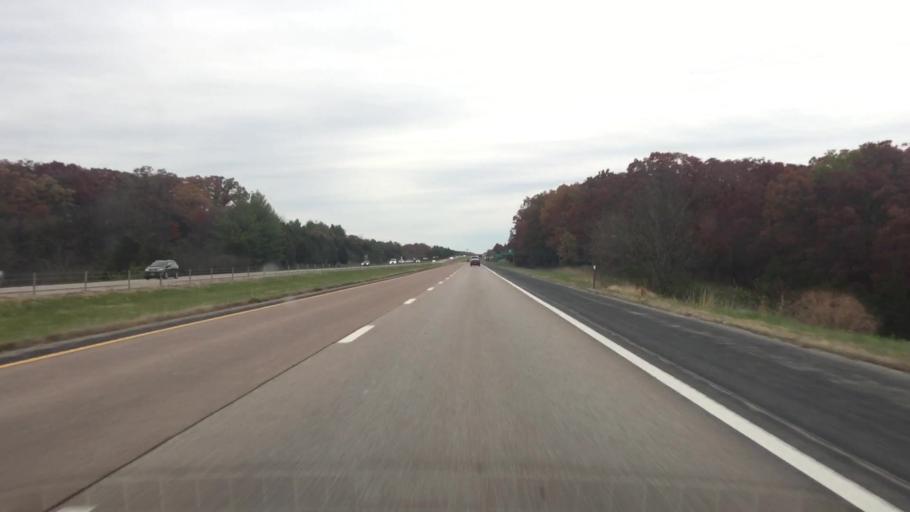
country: US
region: Missouri
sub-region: Boone County
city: Ashland
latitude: 38.7260
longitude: -92.2540
